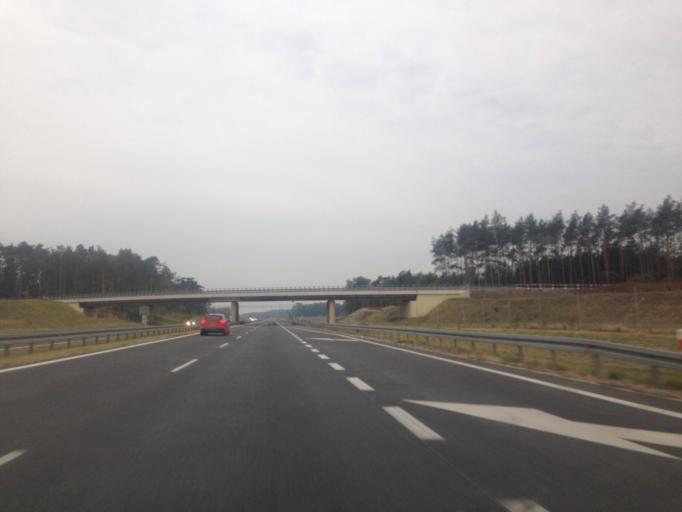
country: PL
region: Greater Poland Voivodeship
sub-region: Powiat poznanski
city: Pobiedziska
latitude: 52.4308
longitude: 17.3252
